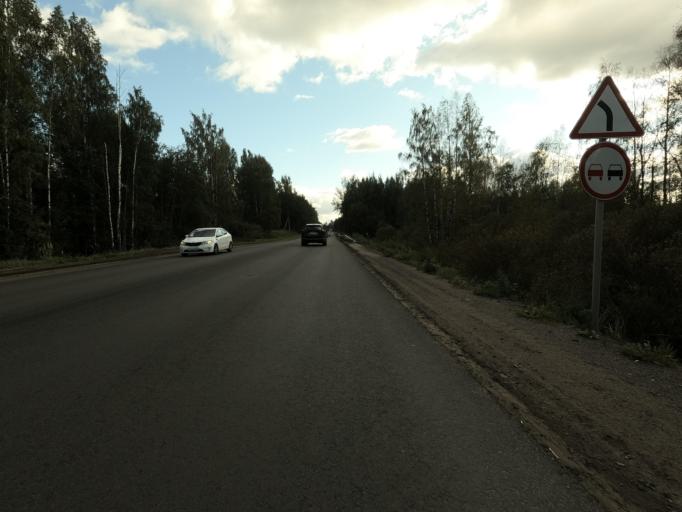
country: RU
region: Leningrad
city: Vsevolozhsk
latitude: 59.9749
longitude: 30.6534
